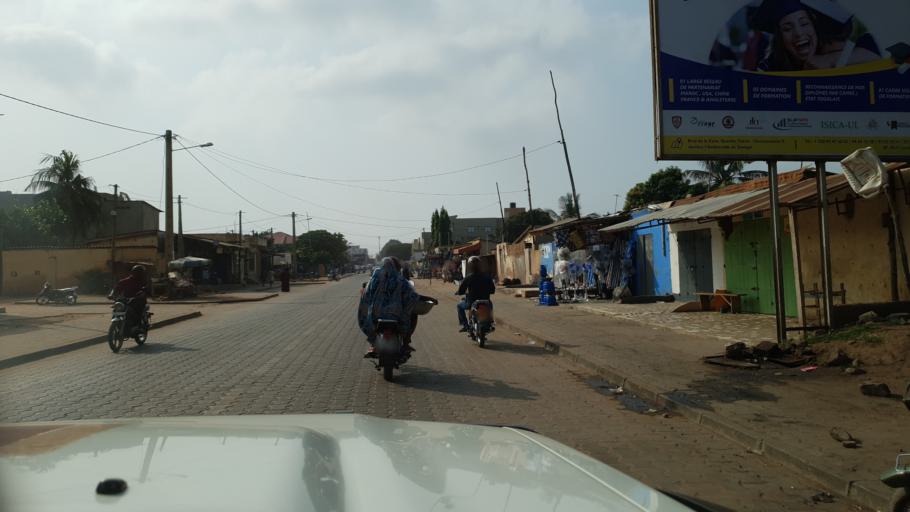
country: TG
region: Maritime
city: Lome
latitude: 6.1598
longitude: 1.2155
